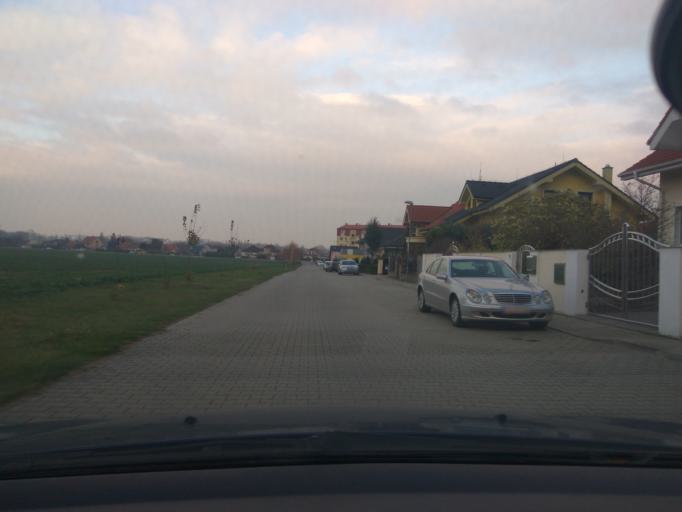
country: SK
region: Trnavsky
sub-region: Okres Trnava
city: Piestany
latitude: 48.5953
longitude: 17.8646
